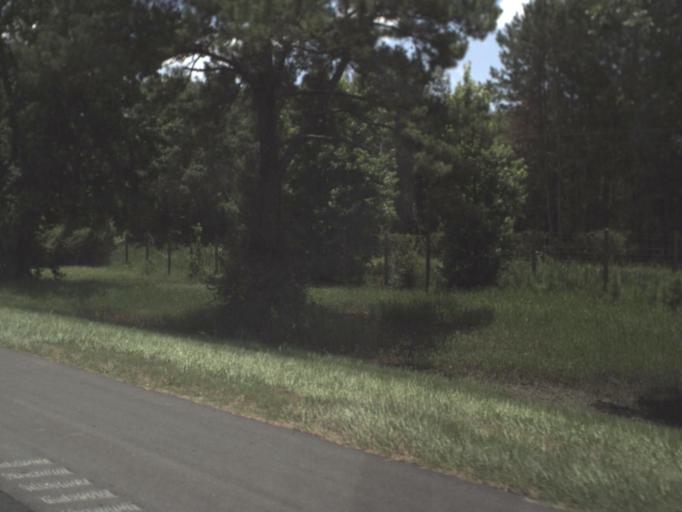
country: US
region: Florida
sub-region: Madison County
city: Madison
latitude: 30.4031
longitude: -83.3903
